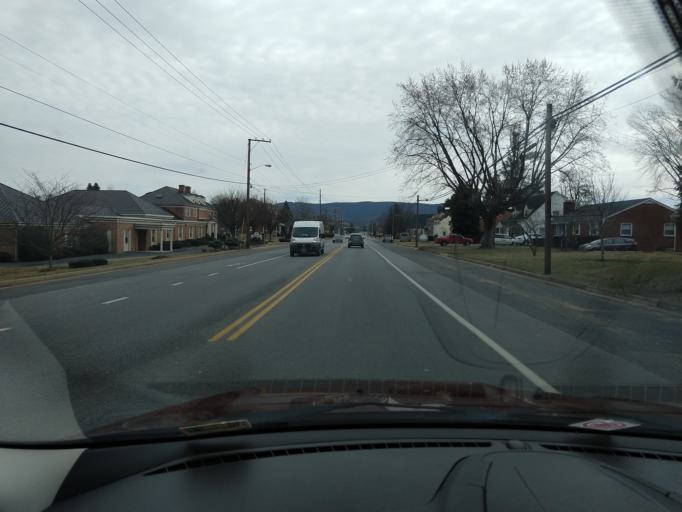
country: US
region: Virginia
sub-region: City of Waynesboro
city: Waynesboro
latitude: 38.0741
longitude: -78.9061
